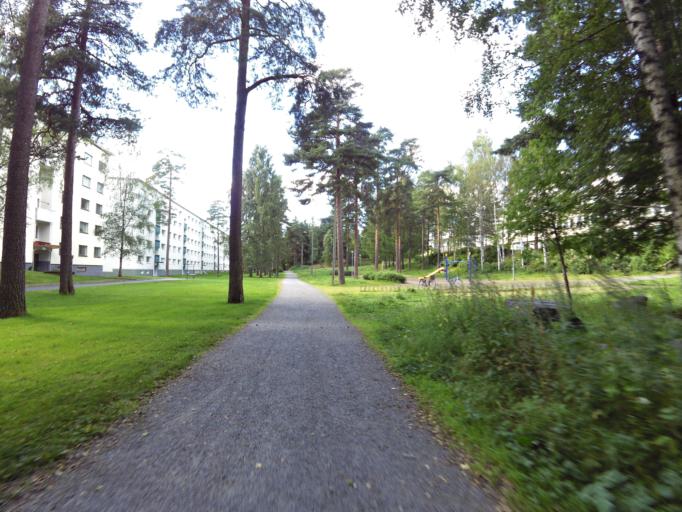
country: FI
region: Pirkanmaa
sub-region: Tampere
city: Pirkkala
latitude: 61.5065
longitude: 23.6219
